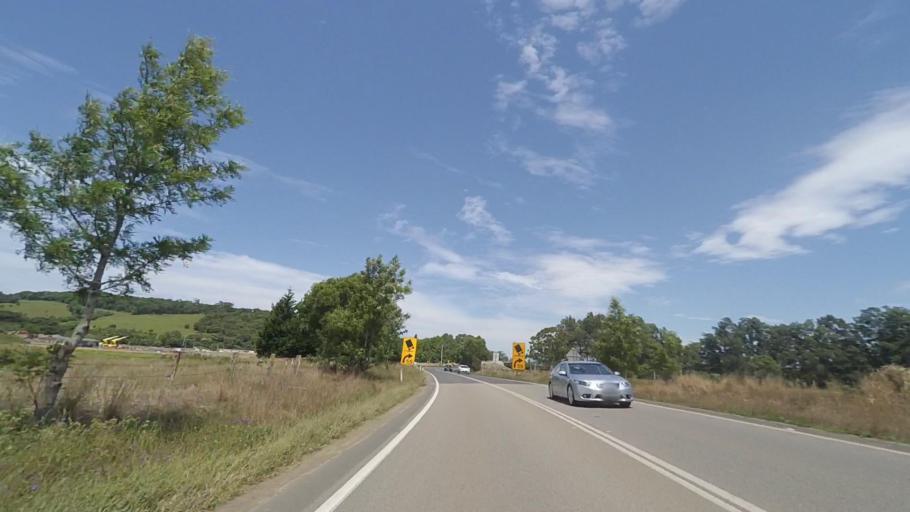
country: AU
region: New South Wales
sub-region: Kiama
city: Gerringong
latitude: -34.7440
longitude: 150.7599
